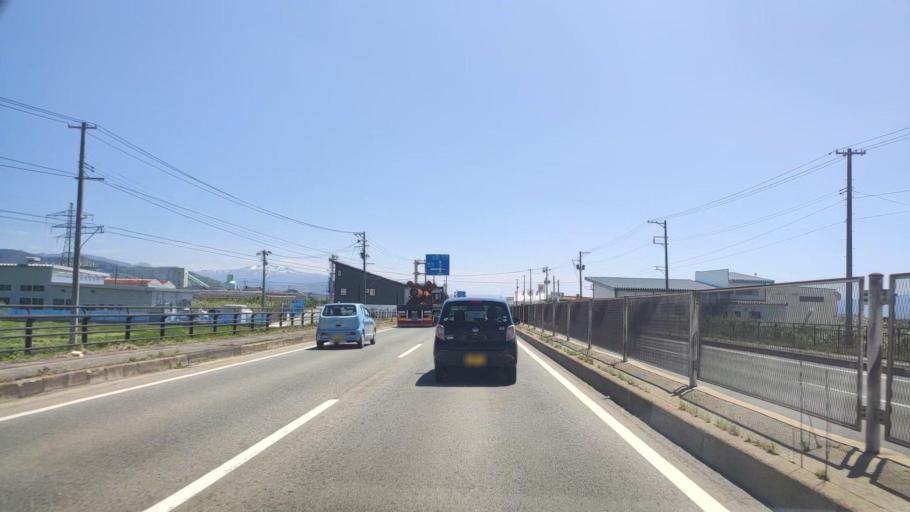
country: JP
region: Yamagata
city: Higashine
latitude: 38.4214
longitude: 140.3758
